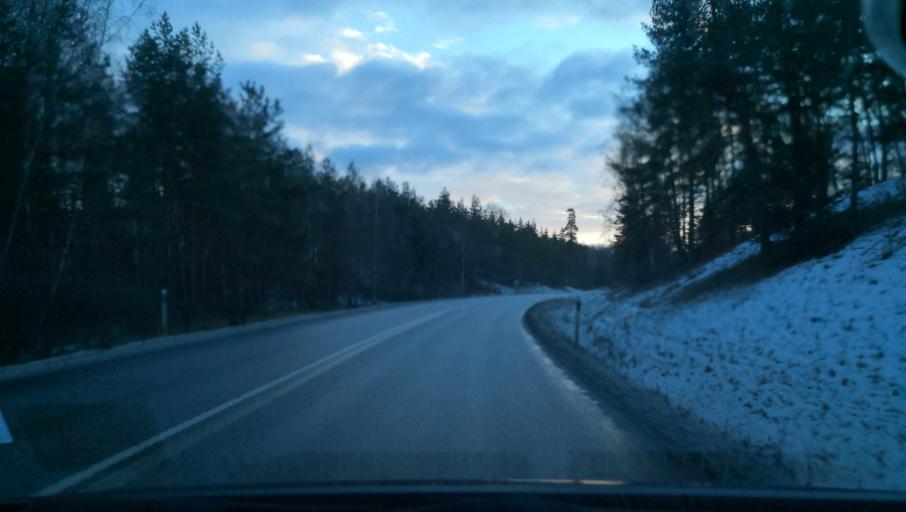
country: SE
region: Soedermanland
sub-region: Eskilstuna Kommun
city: Skogstorp
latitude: 59.3055
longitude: 16.4488
